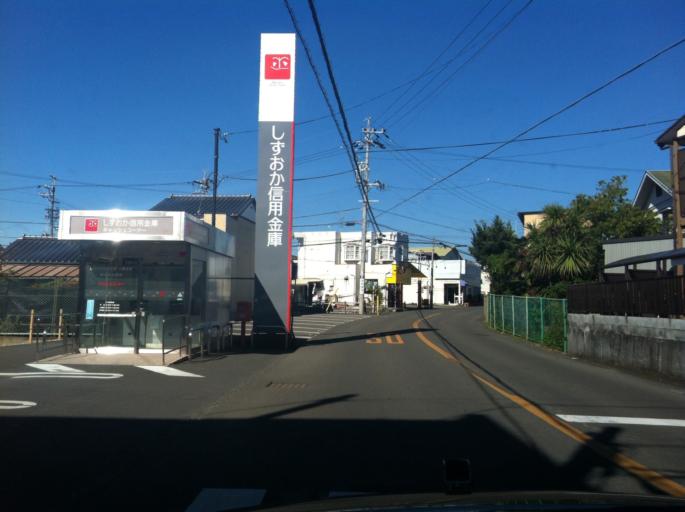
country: JP
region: Shizuoka
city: Shizuoka-shi
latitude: 34.9663
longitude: 138.4260
